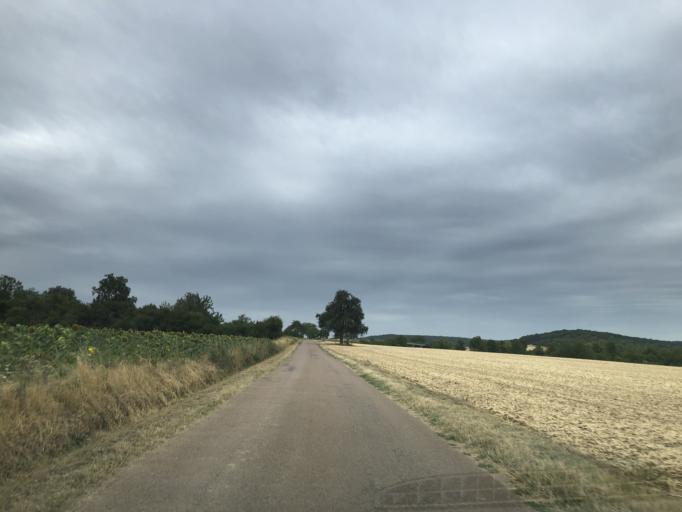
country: FR
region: Bourgogne
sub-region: Departement de l'Yonne
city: Aillant-sur-Tholon
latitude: 47.9101
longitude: 3.3436
